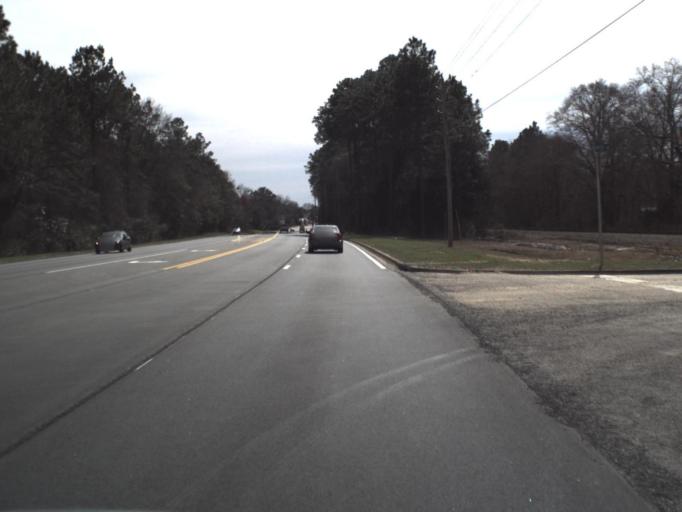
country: US
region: Florida
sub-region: Washington County
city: Chipley
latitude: 30.7019
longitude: -85.3918
